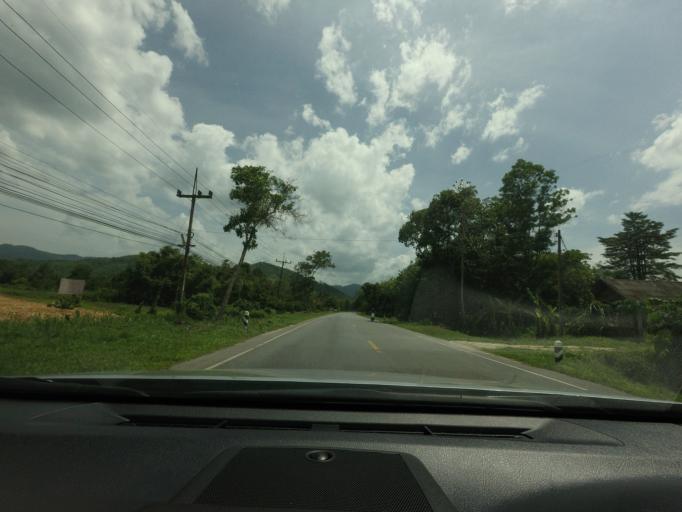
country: TH
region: Yala
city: Raman
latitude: 6.4549
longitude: 101.3537
